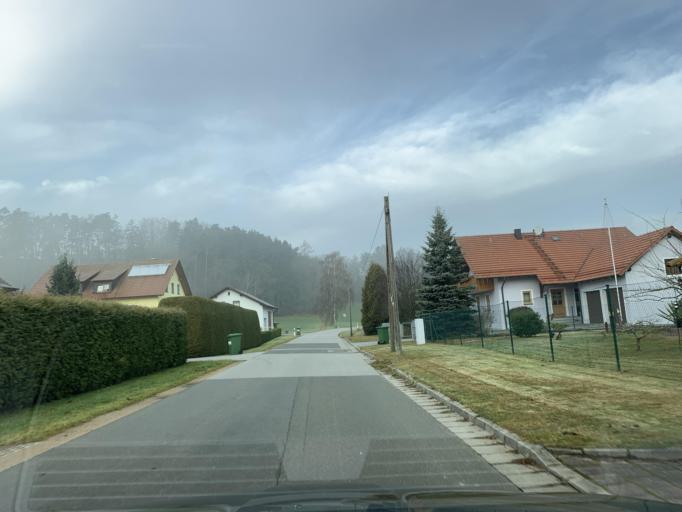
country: DE
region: Bavaria
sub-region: Upper Palatinate
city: Neunburg vorm Wald
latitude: 49.3636
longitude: 12.3963
